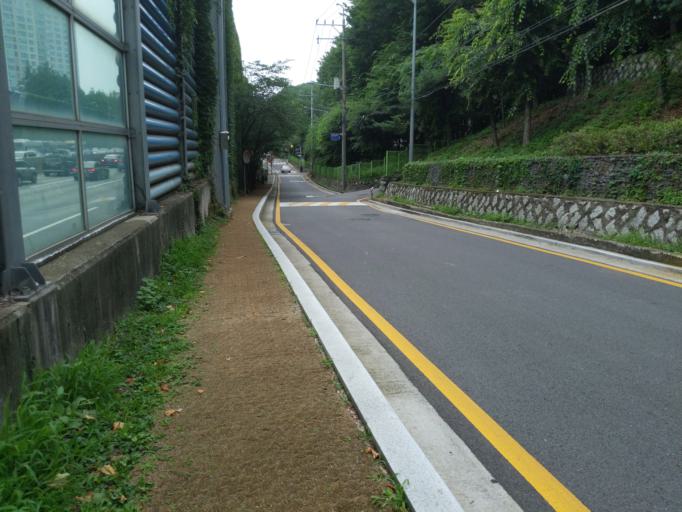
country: KR
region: Seoul
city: Seoul
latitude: 37.5064
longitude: 127.0175
